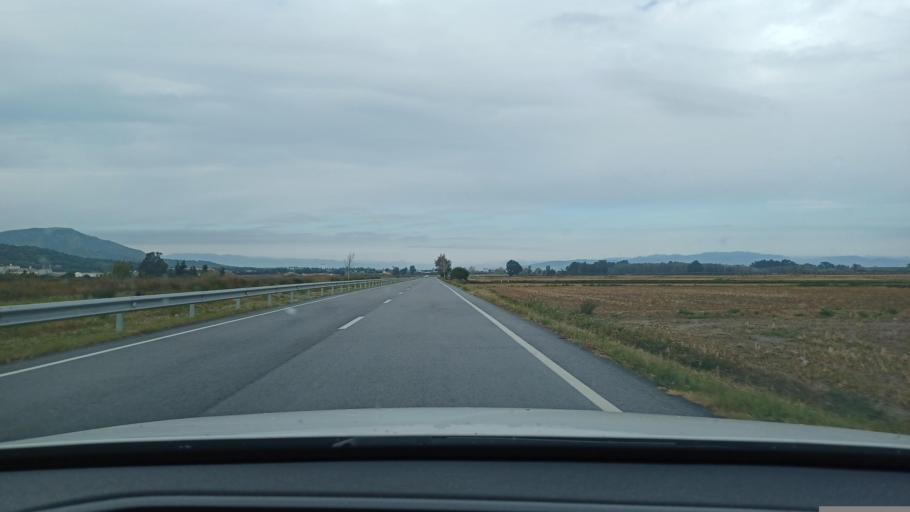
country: ES
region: Catalonia
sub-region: Provincia de Tarragona
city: Sant Carles de la Rapita
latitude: 40.6582
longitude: 0.5933
